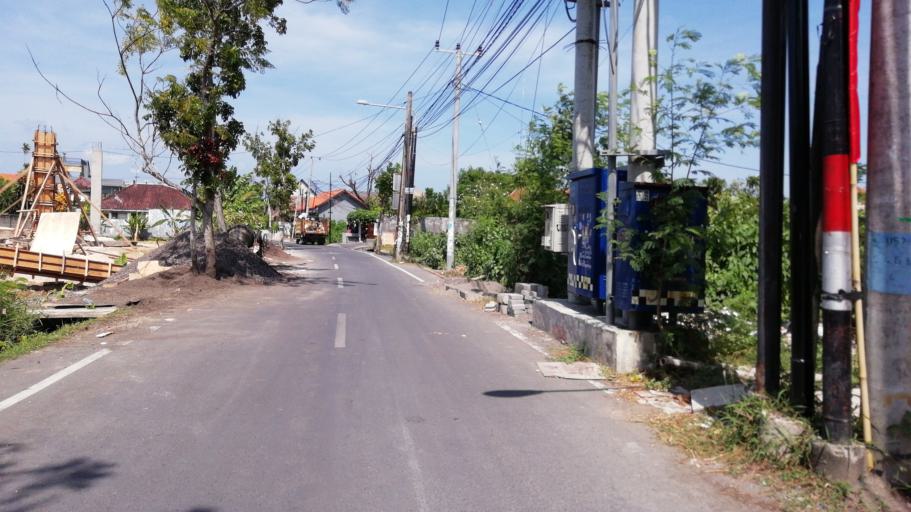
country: ID
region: Bali
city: Banjar Kerobokan
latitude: -8.6603
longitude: 115.1371
